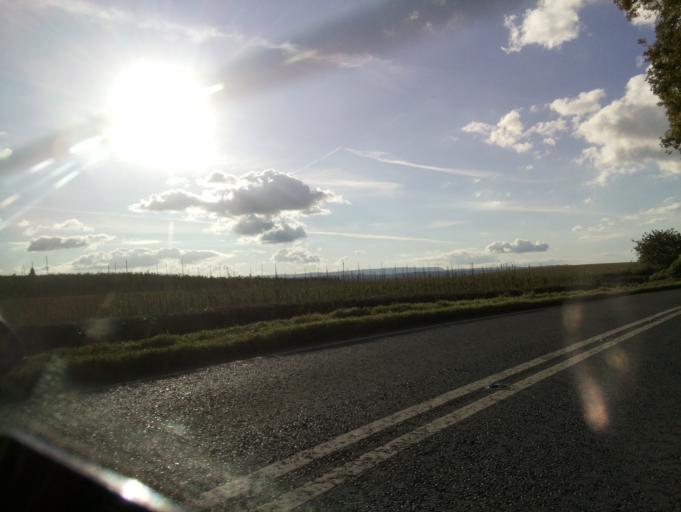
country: GB
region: England
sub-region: Herefordshire
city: Credenhill
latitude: 52.0721
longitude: -2.7957
